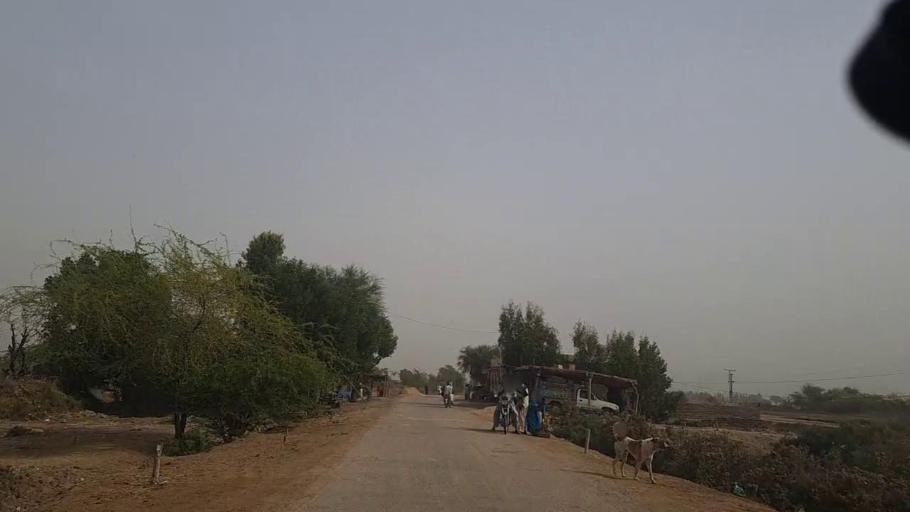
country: PK
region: Sindh
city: Pithoro
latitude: 25.4432
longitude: 69.2959
